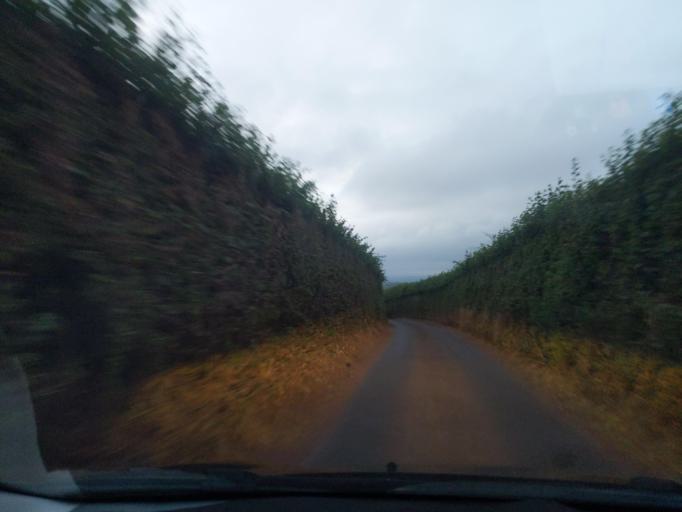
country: GB
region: England
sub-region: Devon
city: Ipplepen
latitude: 50.4760
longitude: -3.6152
